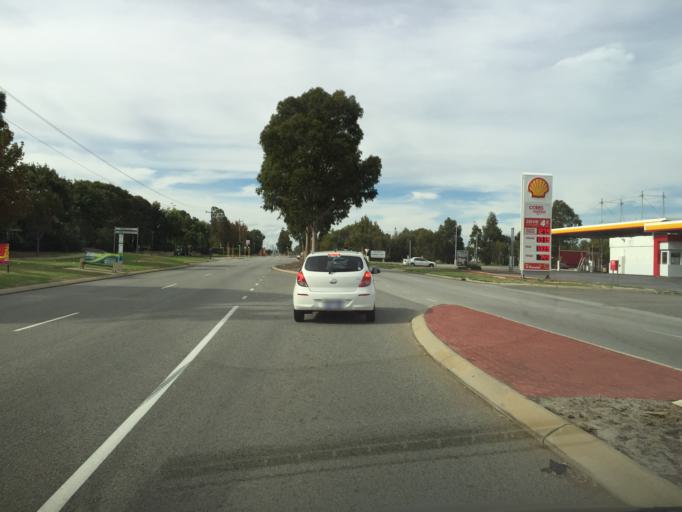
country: AU
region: Western Australia
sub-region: Canning
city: Willetton
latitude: -32.0705
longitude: 115.8948
